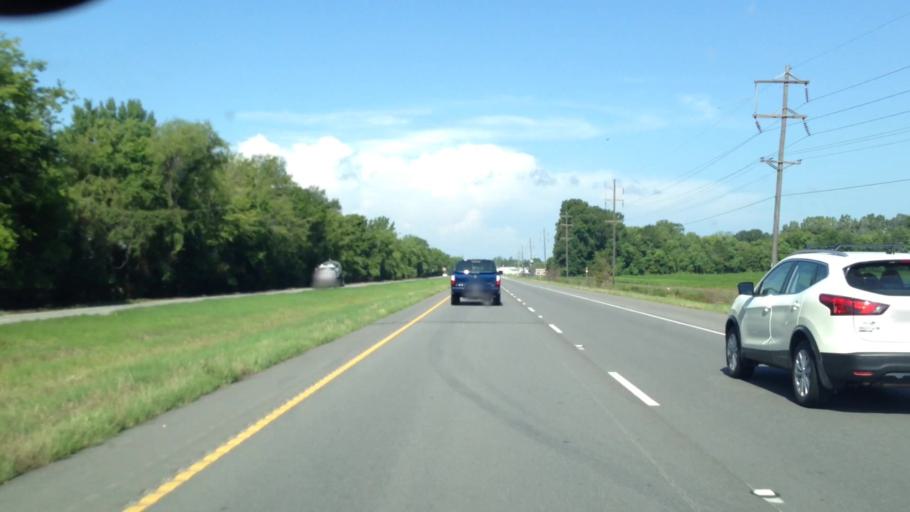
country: US
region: Louisiana
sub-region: Saint Landry Parish
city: Port Barre
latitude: 30.5469
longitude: -91.9499
